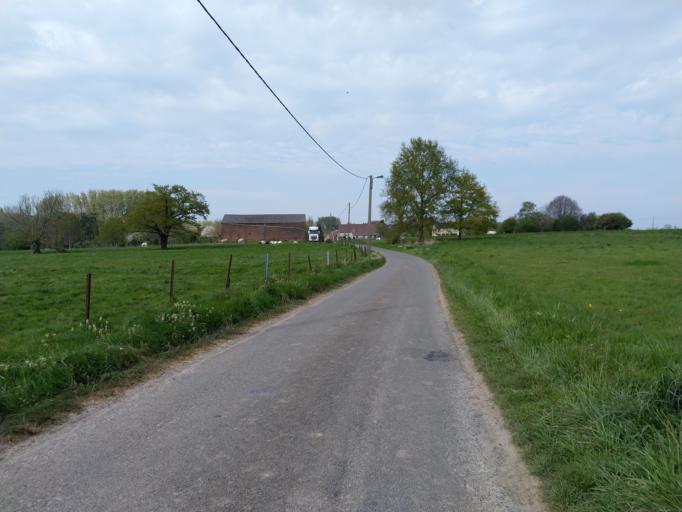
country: BE
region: Wallonia
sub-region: Province du Hainaut
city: Jurbise
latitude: 50.5269
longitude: 3.8850
